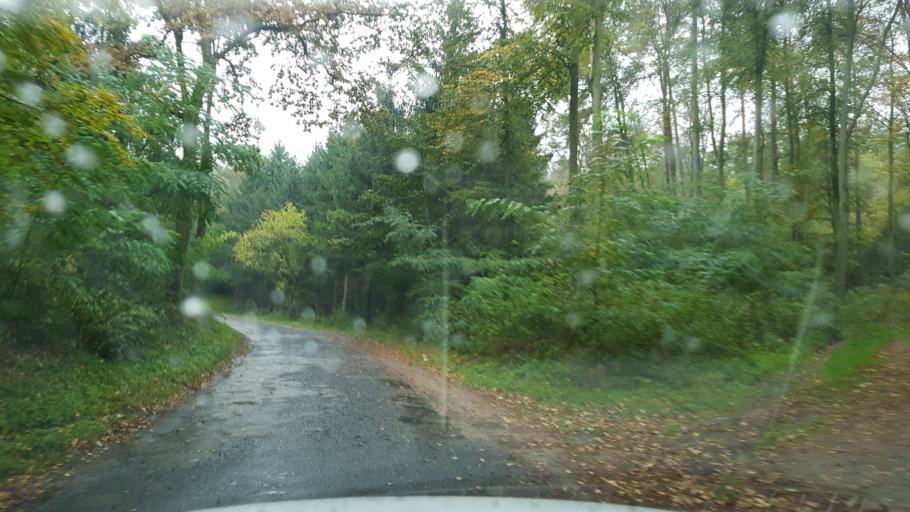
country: PL
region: West Pomeranian Voivodeship
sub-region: Powiat mysliborski
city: Barlinek
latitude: 53.0224
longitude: 15.2212
